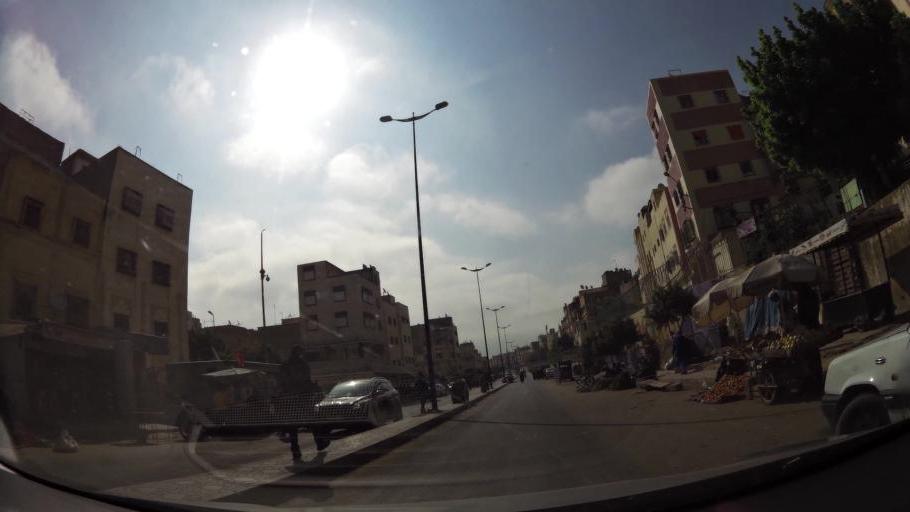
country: MA
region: Fes-Boulemane
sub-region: Fes
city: Fes
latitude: 34.0678
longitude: -5.0125
